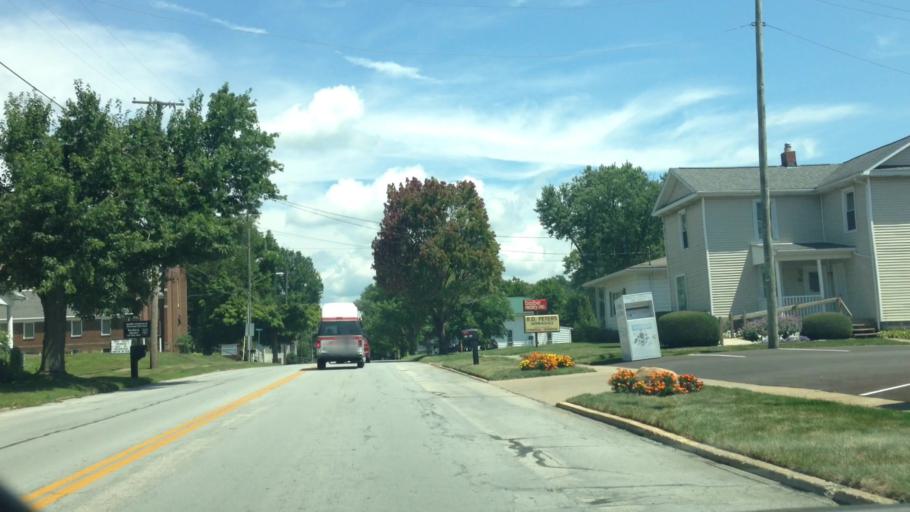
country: US
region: Ohio
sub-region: Wayne County
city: Smithville
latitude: 40.8643
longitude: -81.8580
